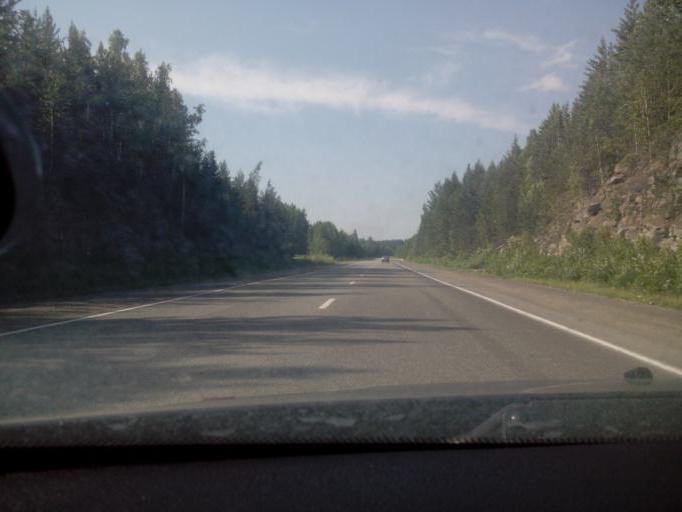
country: RU
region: Sverdlovsk
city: Kalinovo
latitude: 57.1945
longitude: 60.2543
